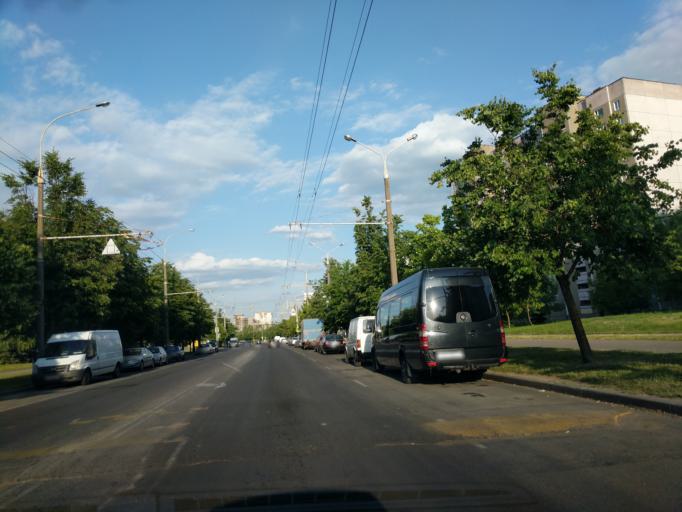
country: BY
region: Minsk
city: Malinovka
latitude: 53.8496
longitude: 27.4611
